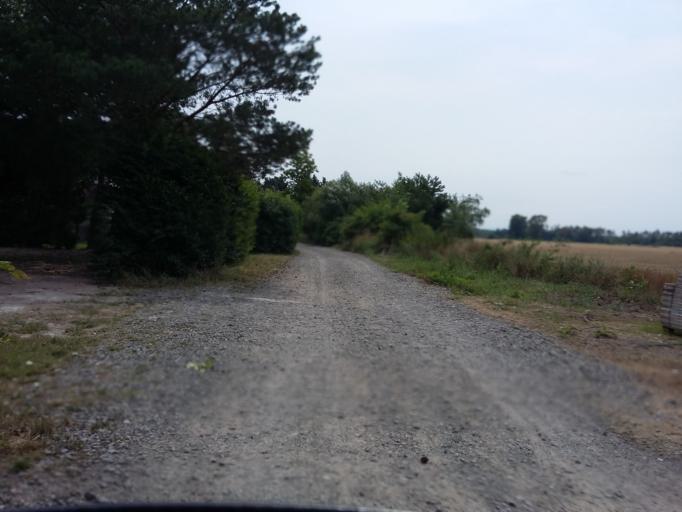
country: AT
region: Lower Austria
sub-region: Politischer Bezirk Ganserndorf
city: Drosing
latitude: 48.4933
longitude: 16.9497
